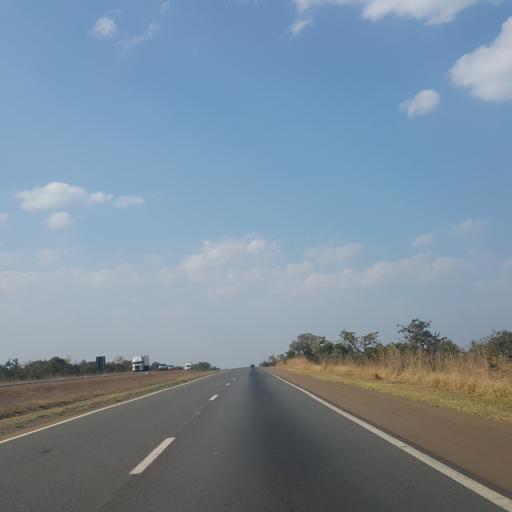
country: BR
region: Goias
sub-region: Abadiania
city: Abadiania
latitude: -16.2005
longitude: -48.7362
